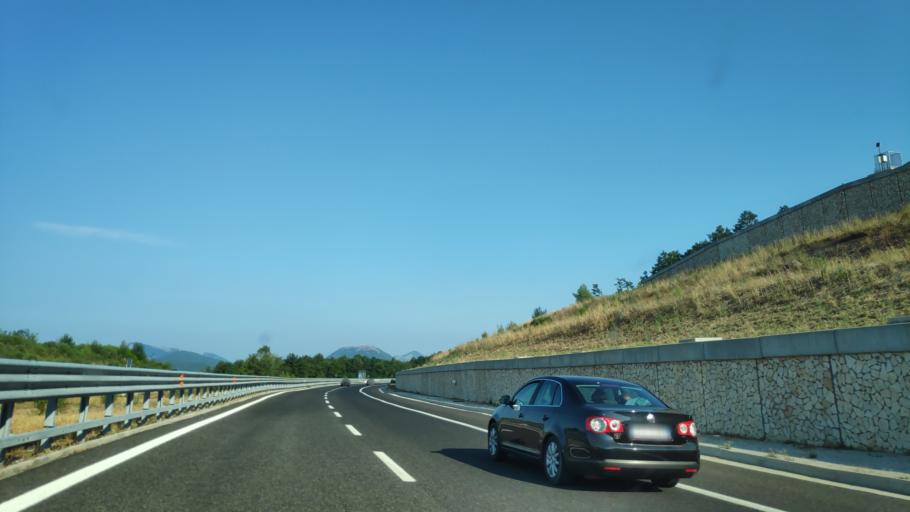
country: IT
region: Basilicate
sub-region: Provincia di Potenza
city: Nemoli
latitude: 40.1019
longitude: 15.7995
